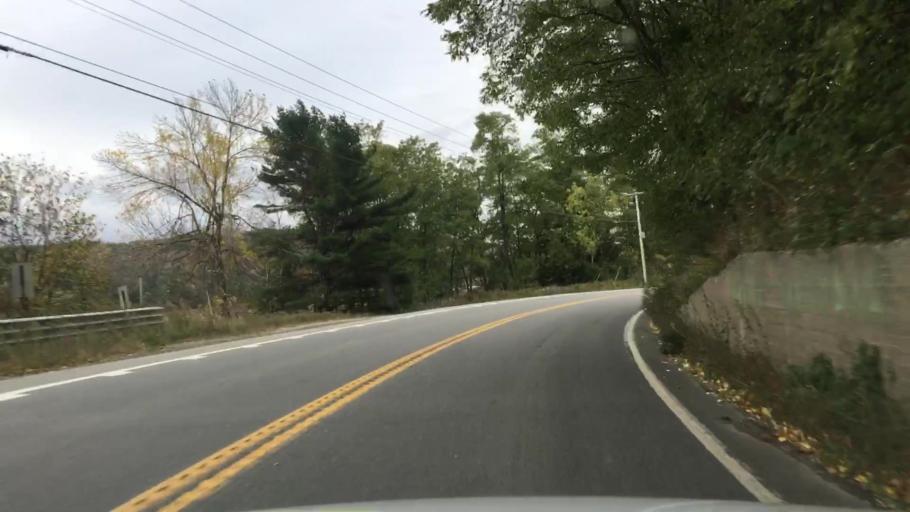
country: US
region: Maine
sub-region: Waldo County
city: Frankfort
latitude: 44.5974
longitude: -68.8657
